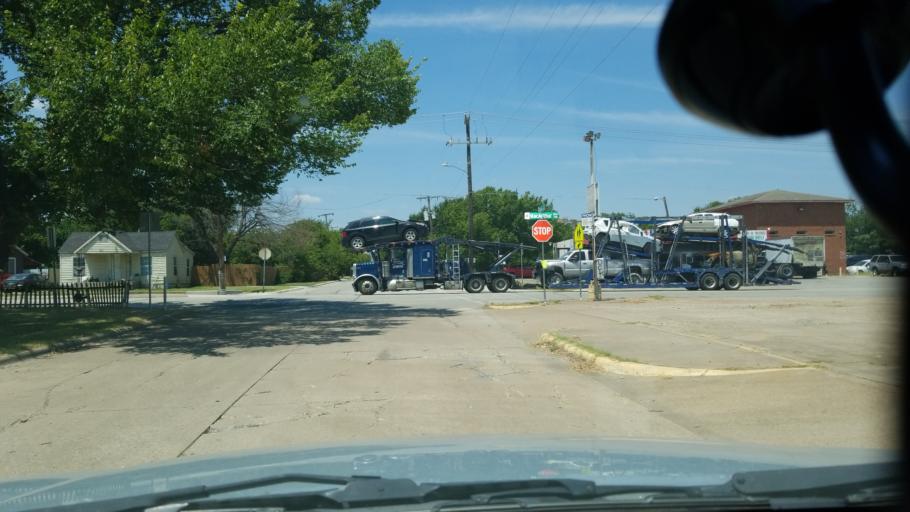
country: US
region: Texas
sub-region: Dallas County
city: Grand Prairie
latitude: 32.7563
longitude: -96.9596
